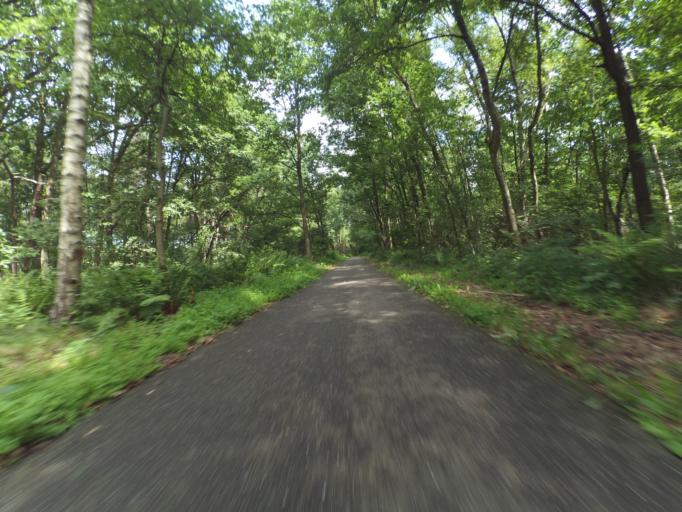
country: BE
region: Flanders
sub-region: Provincie Limburg
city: Maaseik
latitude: 51.0735
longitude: 5.7323
